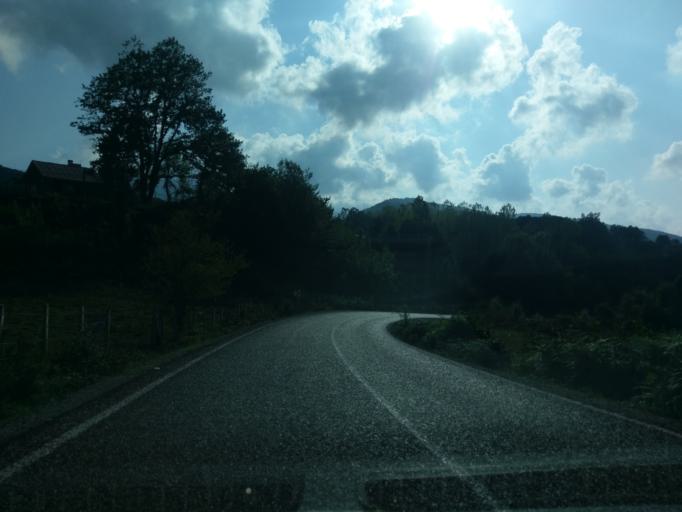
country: TR
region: Sinop
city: Ayancik
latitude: 41.8887
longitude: 34.4939
